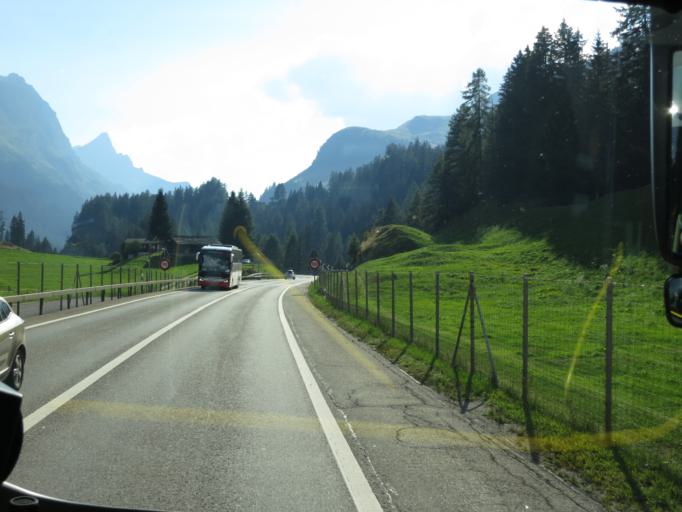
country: CH
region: Grisons
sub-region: Hinterrhein District
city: Hinterrhein
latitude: 46.5604
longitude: 9.3458
